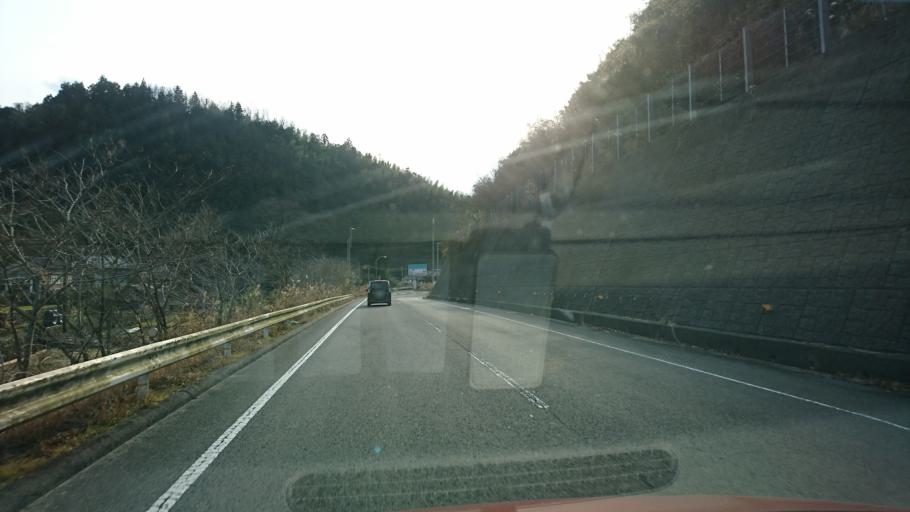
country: JP
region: Ehime
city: Hojo
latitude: 33.9182
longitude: 132.8855
